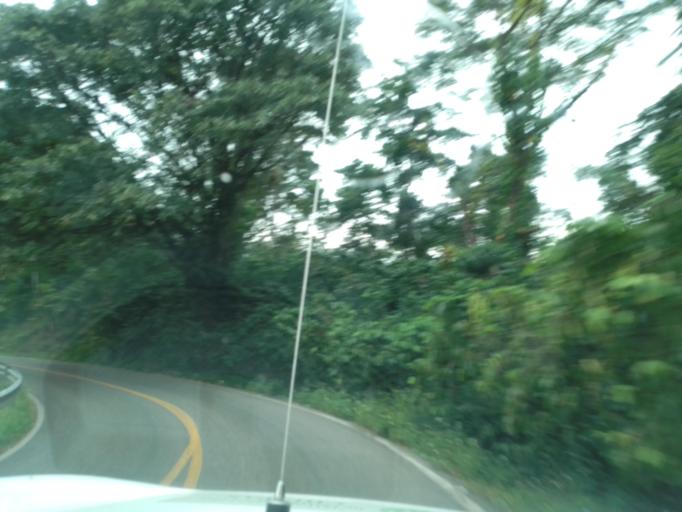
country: MX
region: Chiapas
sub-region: Union Juarez
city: Santo Domingo
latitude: 15.0382
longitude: -92.1225
